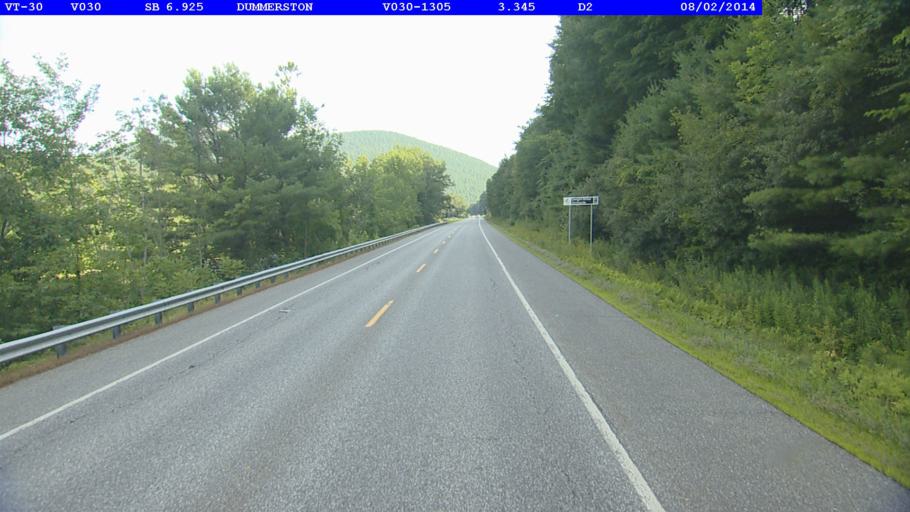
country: US
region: Vermont
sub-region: Windham County
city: Newfane
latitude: 42.9403
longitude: -72.6153
